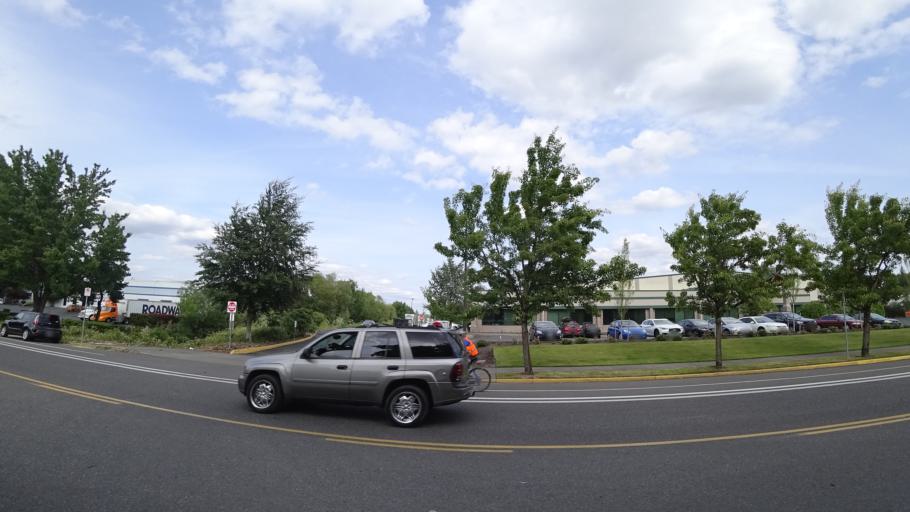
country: US
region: Washington
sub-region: Clark County
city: Vancouver
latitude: 45.5809
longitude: -122.6334
